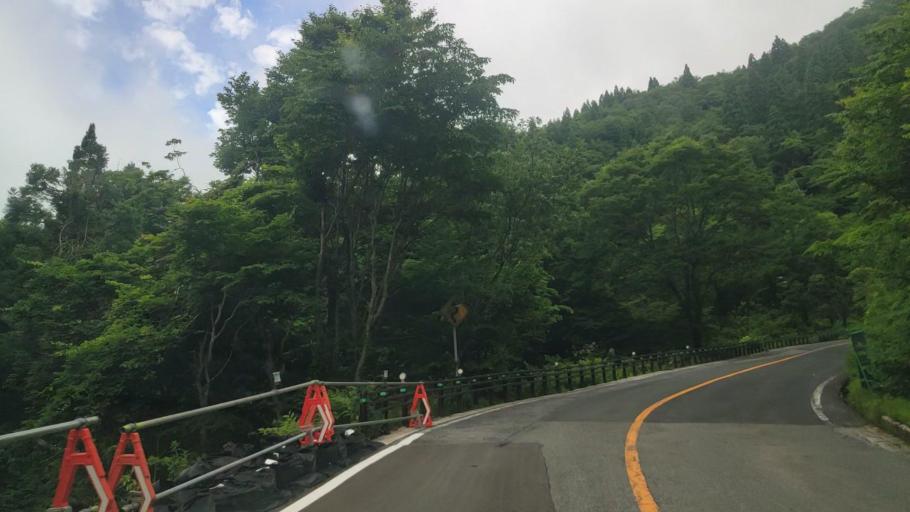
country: JP
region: Tottori
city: Yonago
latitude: 35.3501
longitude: 133.5480
